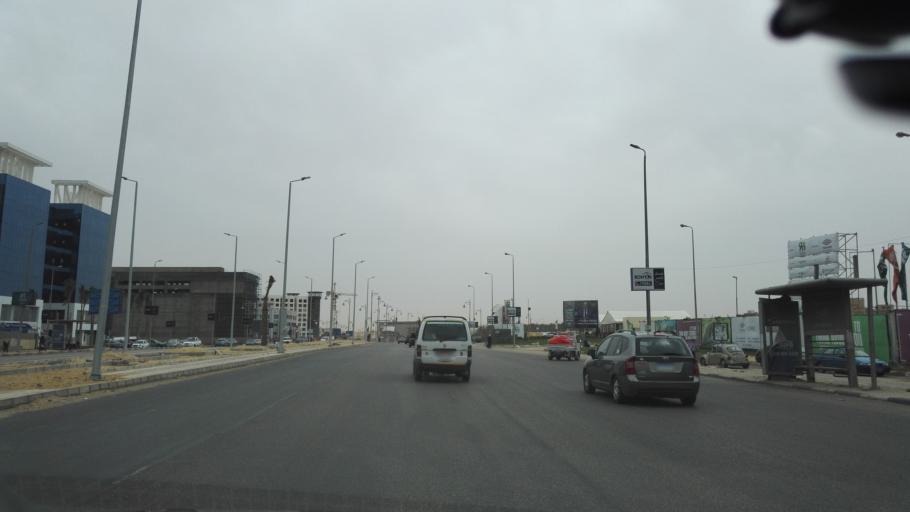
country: EG
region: Muhafazat al Qalyubiyah
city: Al Khankah
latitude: 30.0252
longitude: 31.4922
